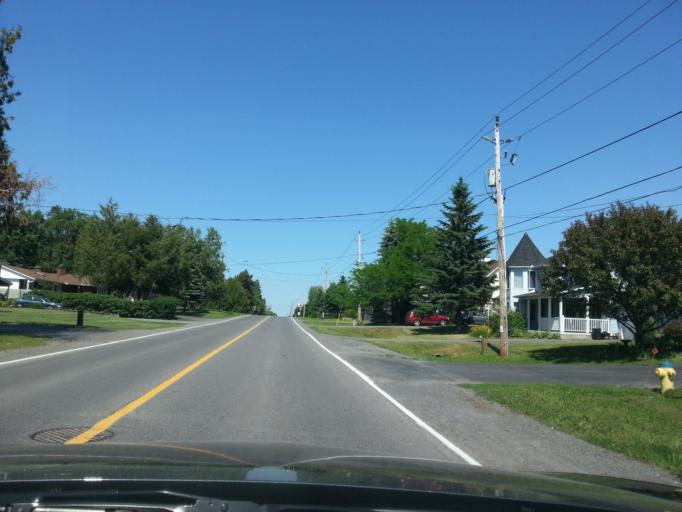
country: CA
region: Ontario
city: Bells Corners
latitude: 45.2455
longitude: -75.9162
